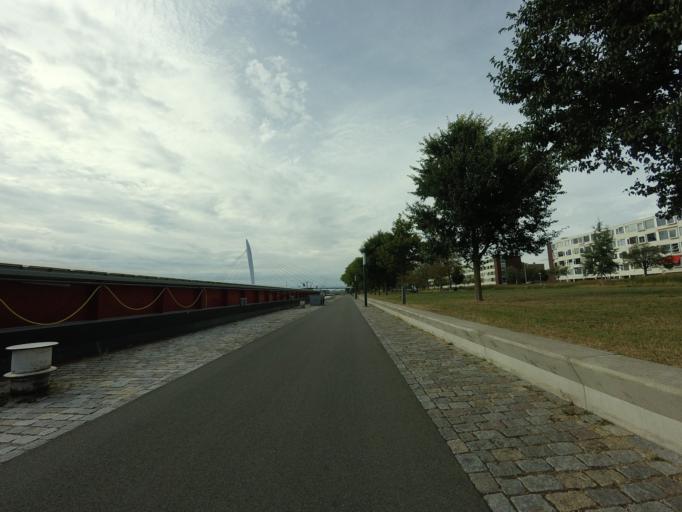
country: NL
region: Utrecht
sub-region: Gemeente Utrecht
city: Utrecht
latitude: 52.0678
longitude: 5.0921
